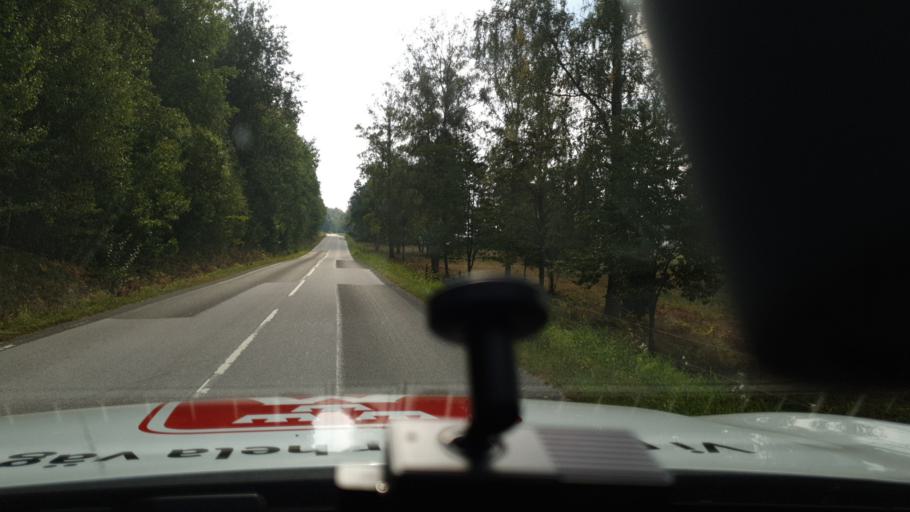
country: SE
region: Kalmar
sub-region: Vimmerby Kommun
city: Sodra Vi
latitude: 57.7406
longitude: 15.8333
